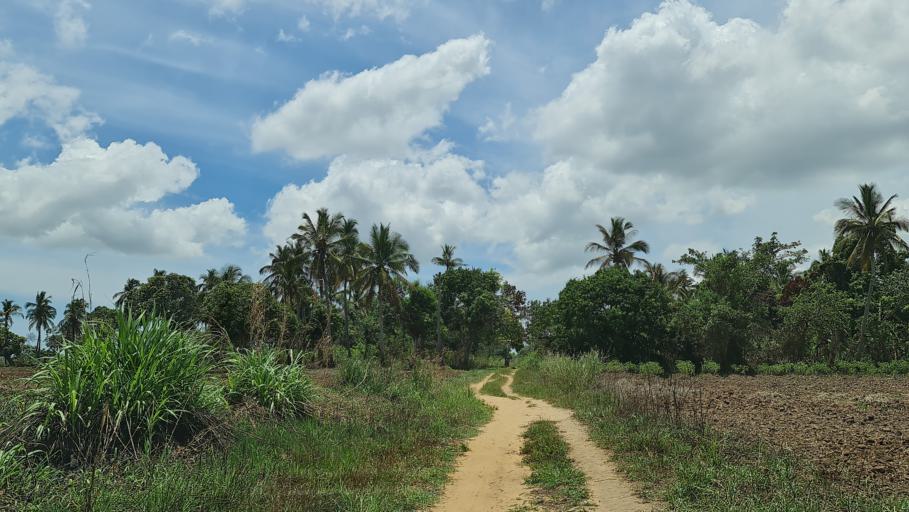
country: MZ
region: Zambezia
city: Quelimane
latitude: -17.5780
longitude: 37.3744
